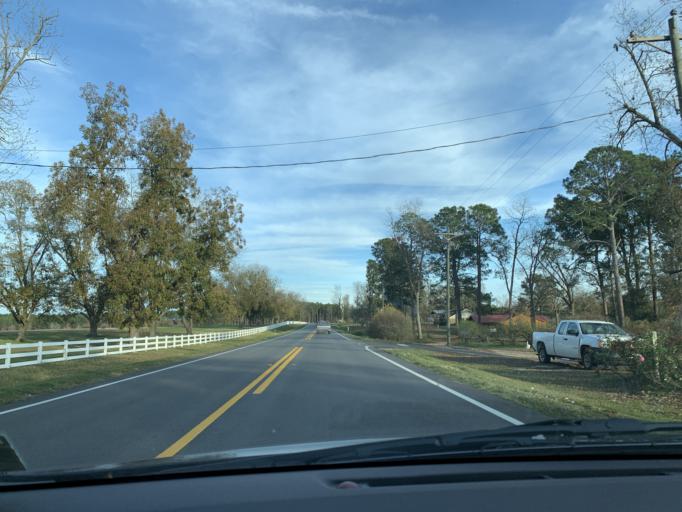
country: US
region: Georgia
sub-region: Irwin County
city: Ocilla
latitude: 31.5927
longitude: -83.2121
